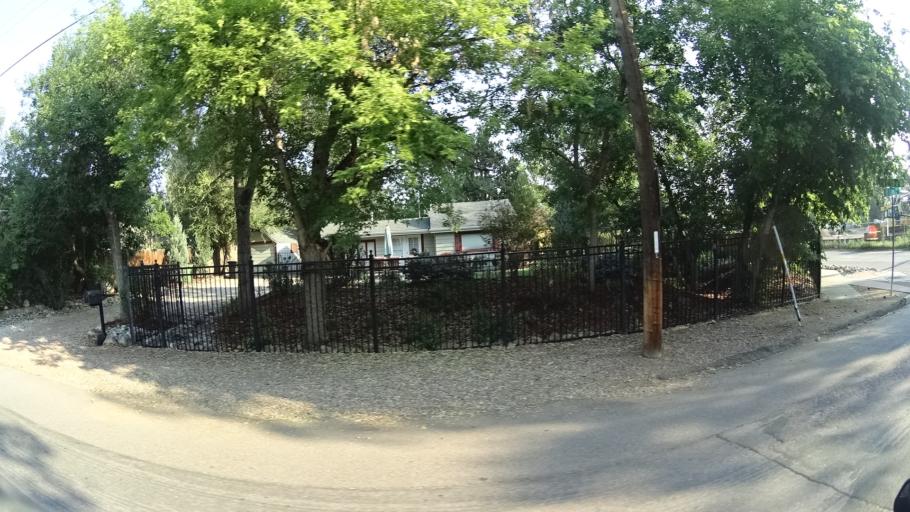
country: US
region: Colorado
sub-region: El Paso County
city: Colorado Springs
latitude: 38.8082
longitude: -104.8267
